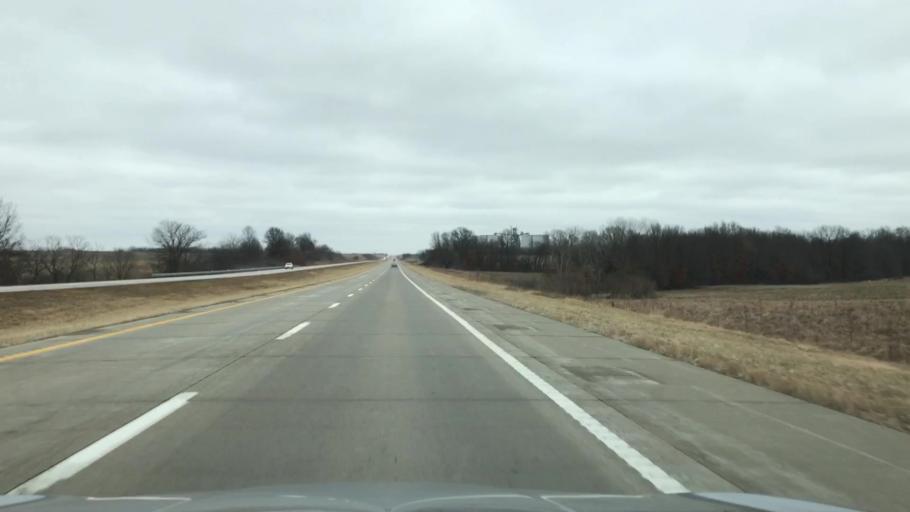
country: US
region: Missouri
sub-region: Caldwell County
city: Hamilton
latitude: 39.7354
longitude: -93.9219
